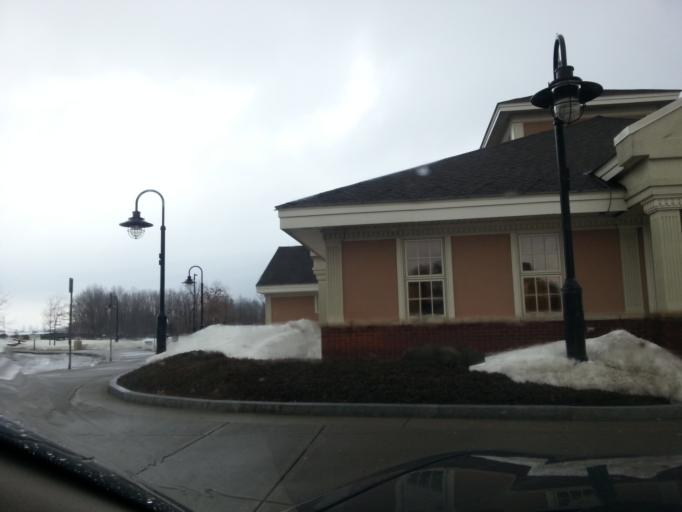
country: US
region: New York
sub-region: Cortland County
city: Homer
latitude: 42.7152
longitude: -76.1460
